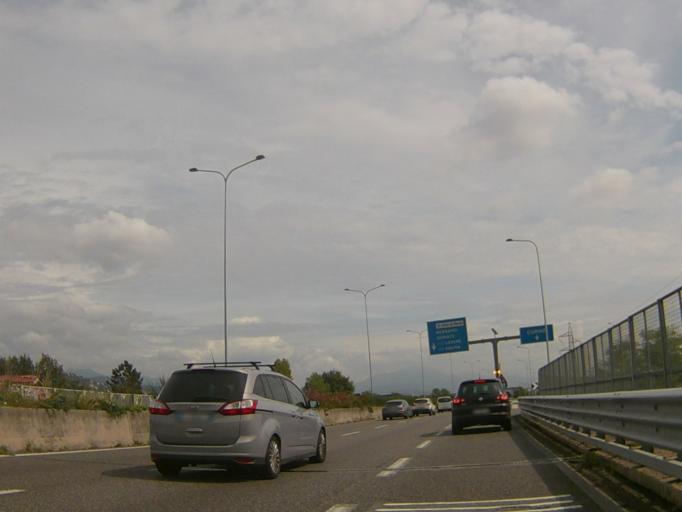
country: IT
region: Lombardy
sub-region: Provincia di Bergamo
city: Treviolo
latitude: 45.6810
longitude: 9.6180
